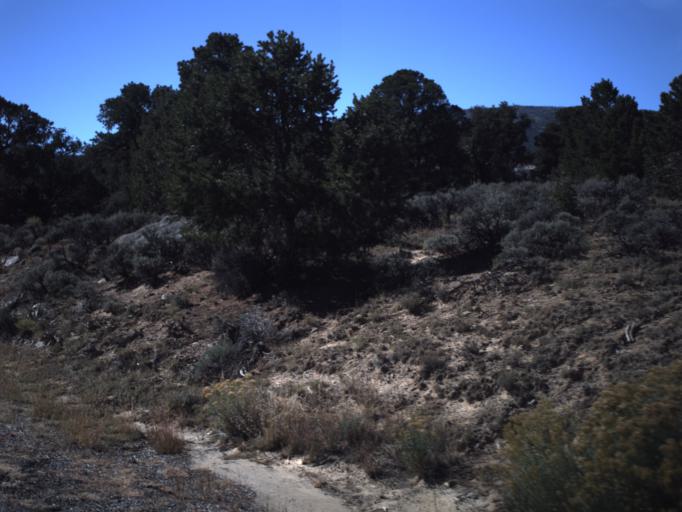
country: US
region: Utah
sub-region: Wayne County
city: Loa
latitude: 38.2427
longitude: -111.3771
